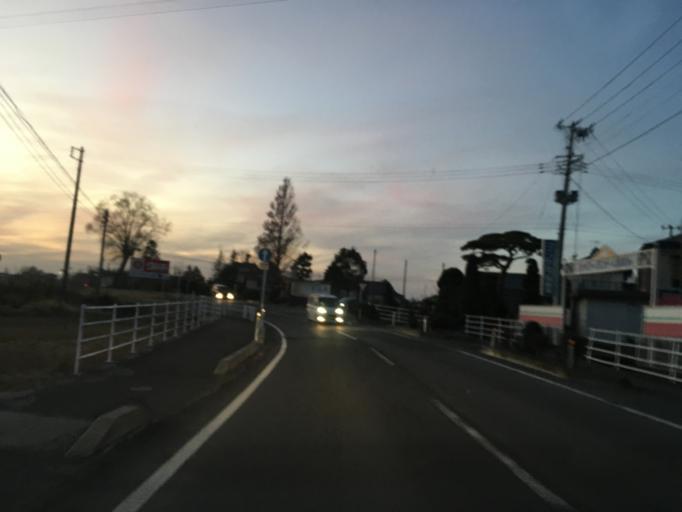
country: JP
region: Miyagi
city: Wakuya
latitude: 38.7126
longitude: 141.2331
